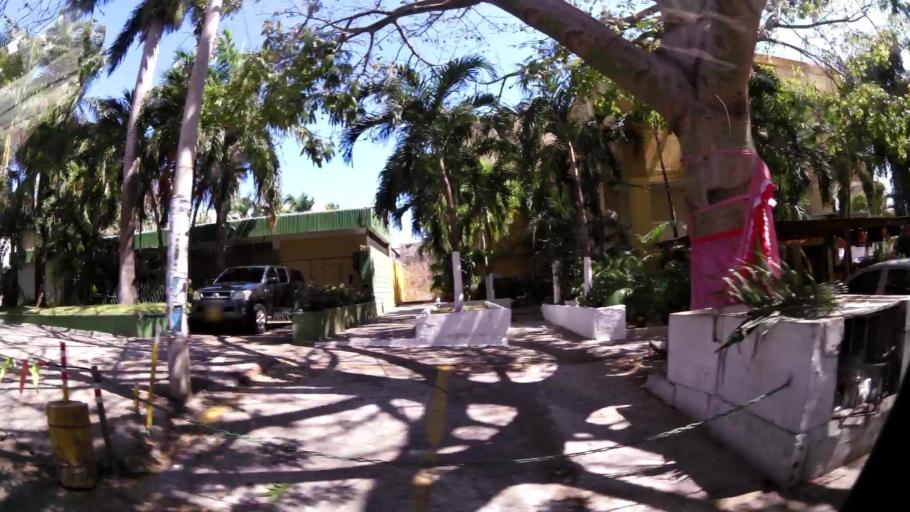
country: CO
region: Atlantico
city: Barranquilla
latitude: 11.0026
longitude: -74.8068
